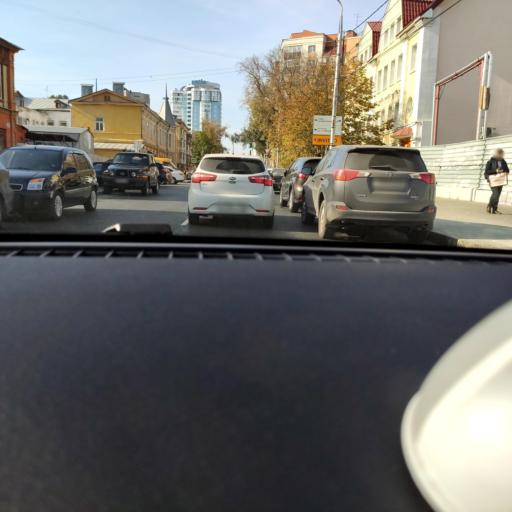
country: RU
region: Samara
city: Samara
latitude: 53.1991
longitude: 50.1089
